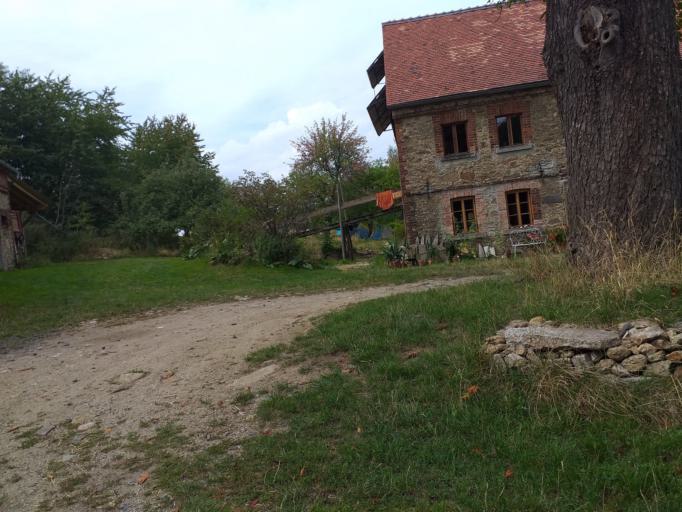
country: PL
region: Lower Silesian Voivodeship
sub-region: Powiat lubanski
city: Lesna
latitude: 51.0009
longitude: 15.3143
